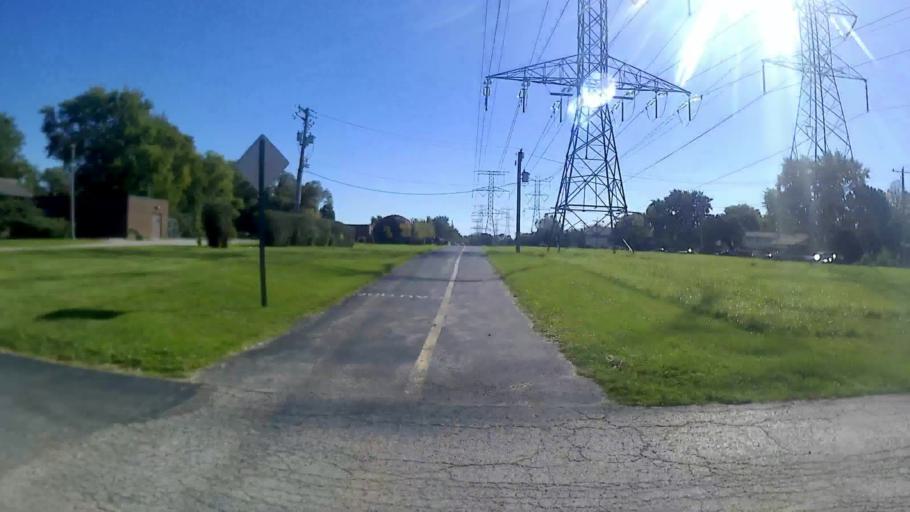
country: US
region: Illinois
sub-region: DuPage County
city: Wood Dale
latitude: 41.9623
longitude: -87.9937
